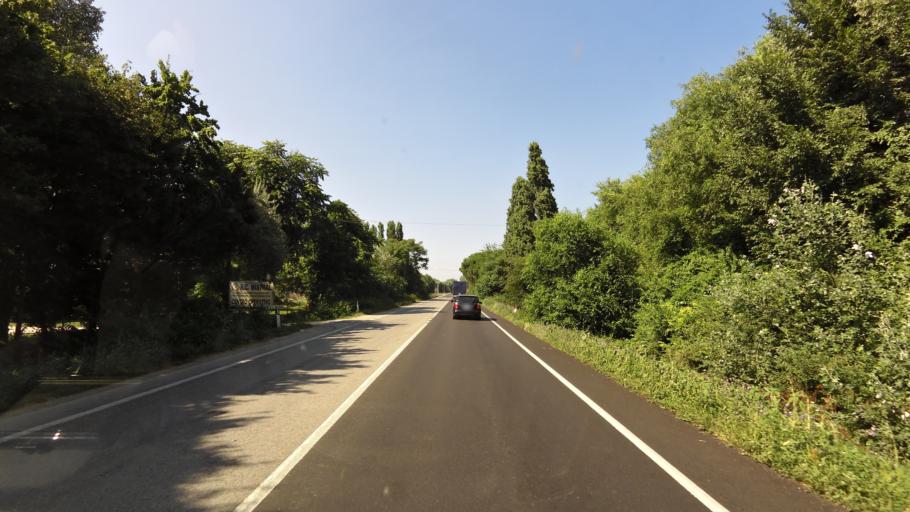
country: IT
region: Emilia-Romagna
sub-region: Provincia di Ravenna
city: Ravenna
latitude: 44.4766
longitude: 12.2102
